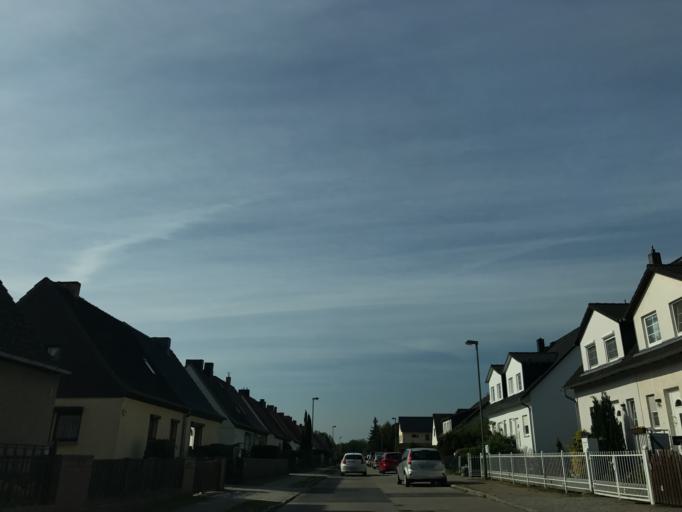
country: DE
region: Berlin
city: Staaken
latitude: 52.5428
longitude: 13.1357
